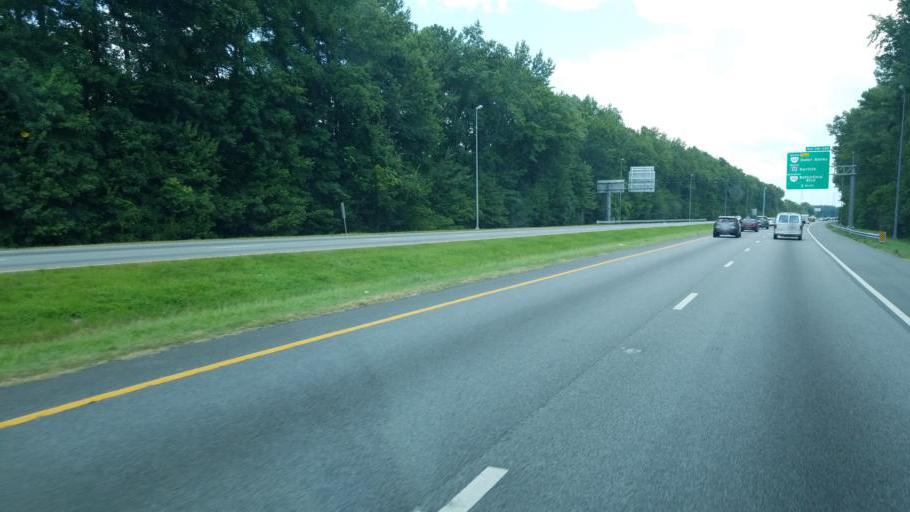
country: US
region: Virginia
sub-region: City of Portsmouth
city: Portsmouth Heights
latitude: 36.7595
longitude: -76.3255
